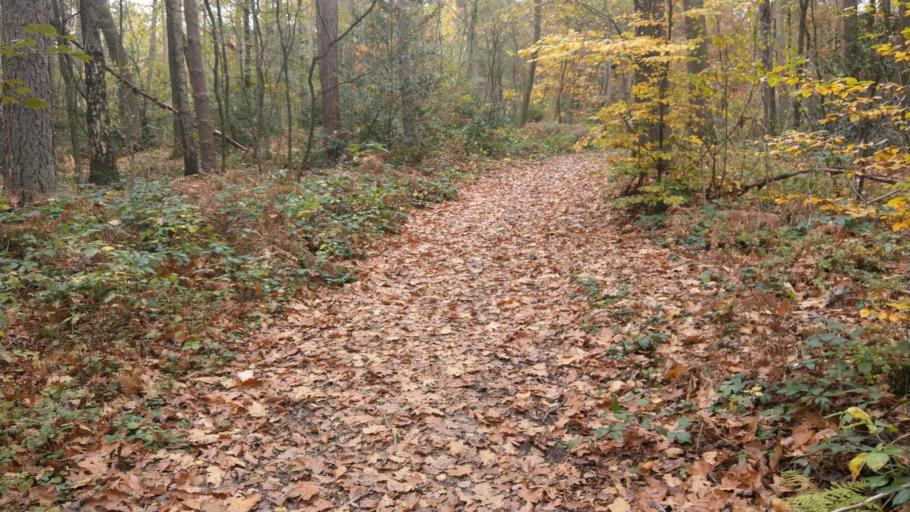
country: BE
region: Wallonia
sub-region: Province de Liege
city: La Calamine
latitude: 50.7339
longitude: 6.0028
